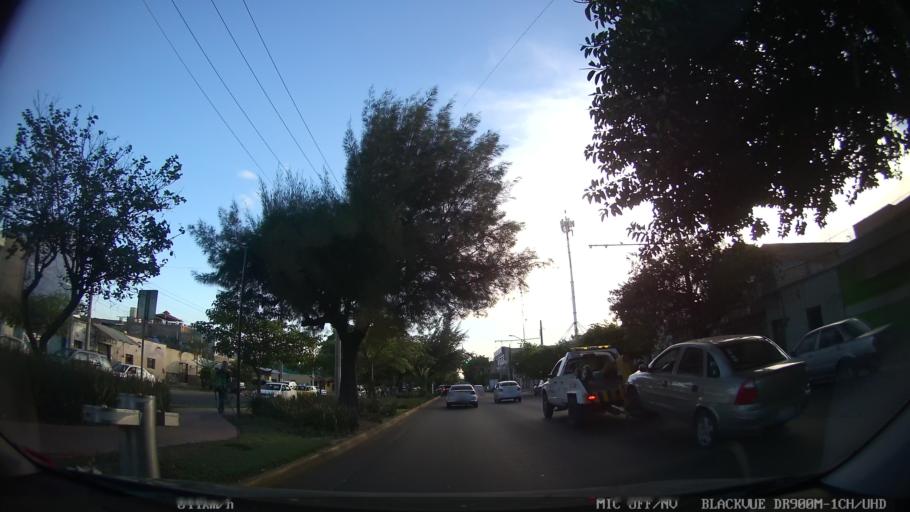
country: MX
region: Jalisco
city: Tlaquepaque
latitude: 20.6964
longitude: -103.2996
